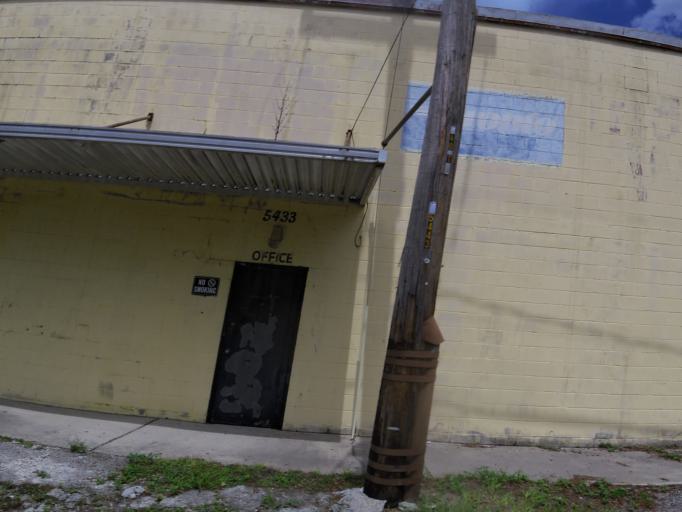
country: US
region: Florida
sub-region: Duval County
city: Jacksonville
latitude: 30.3741
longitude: -81.6402
